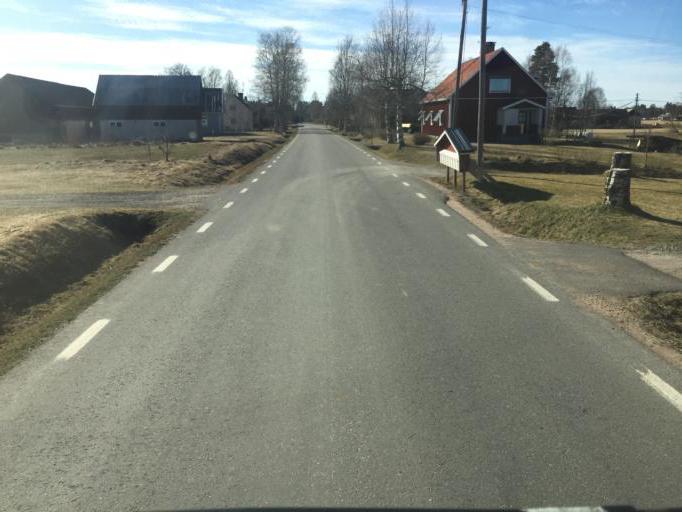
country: SE
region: Dalarna
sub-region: Vansbro Kommun
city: Vansbro
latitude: 60.4595
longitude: 13.9939
